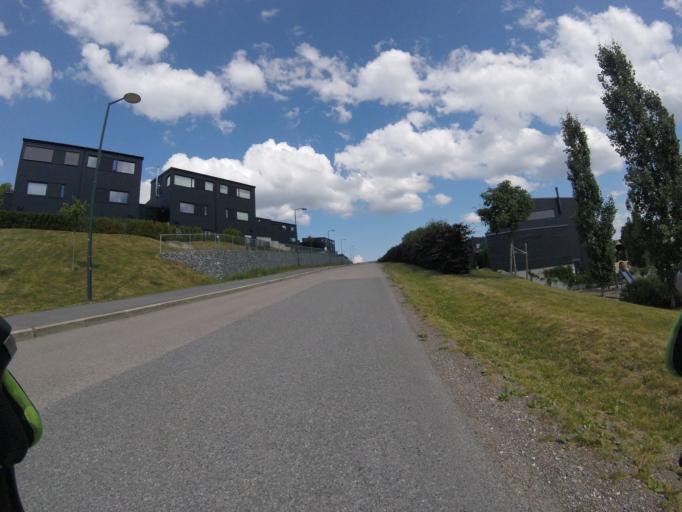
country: NO
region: Akershus
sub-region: Skedsmo
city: Lillestrom
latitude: 59.9750
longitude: 11.0404
